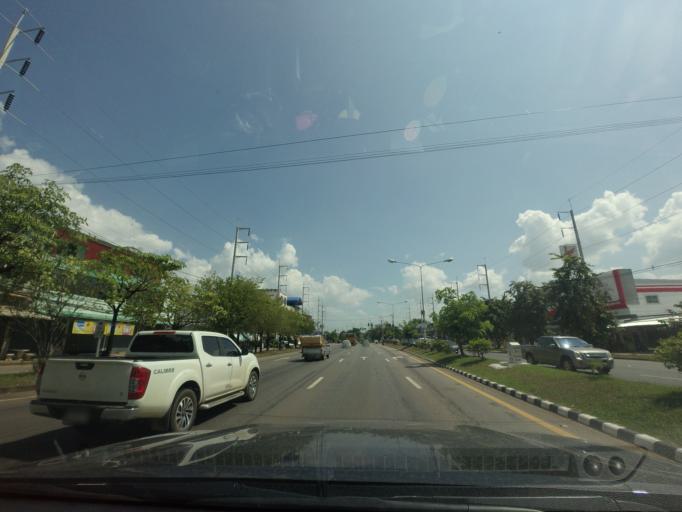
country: TH
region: Phetchabun
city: Nong Phai
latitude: 16.0820
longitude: 101.0575
